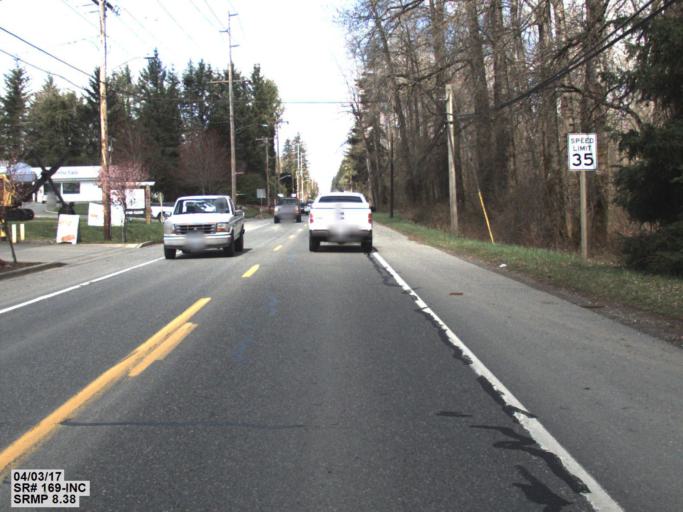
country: US
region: Washington
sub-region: King County
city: Black Diamond
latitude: 47.3191
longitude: -122.0052
